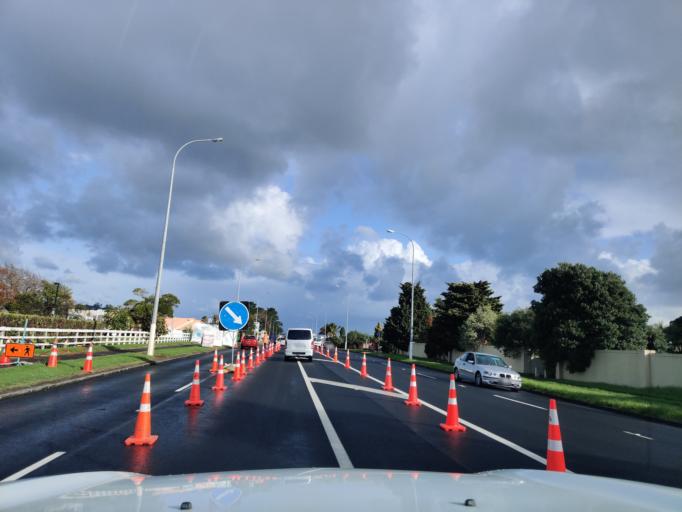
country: NZ
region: Auckland
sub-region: Auckland
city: Pakuranga
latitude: -36.9203
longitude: 174.9130
